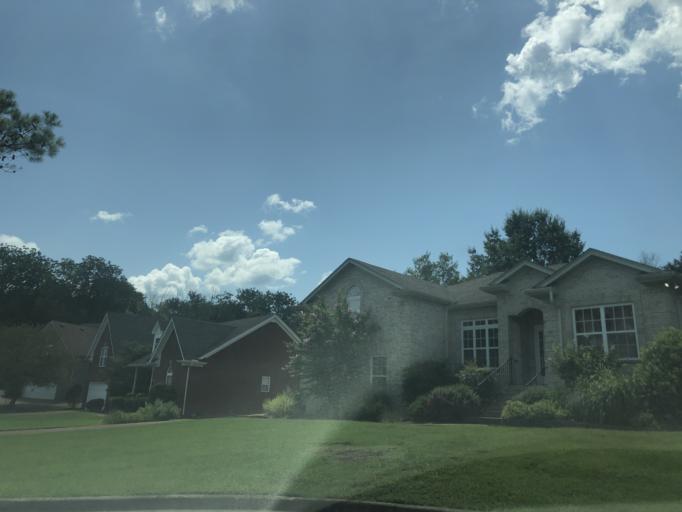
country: US
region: Tennessee
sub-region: Wilson County
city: Green Hill
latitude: 36.1590
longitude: -86.5845
